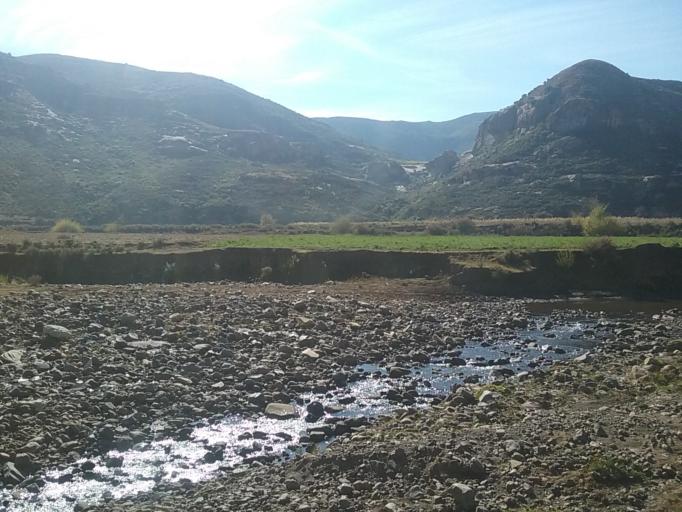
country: LS
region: Berea
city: Teyateyaneng
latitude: -29.2495
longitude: 27.9244
